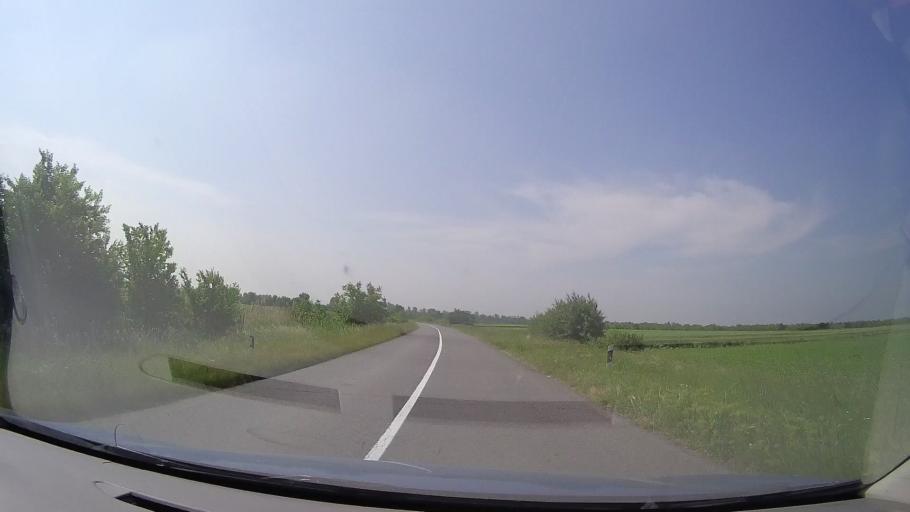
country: RS
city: Jarkovac
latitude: 45.2816
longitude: 20.7626
